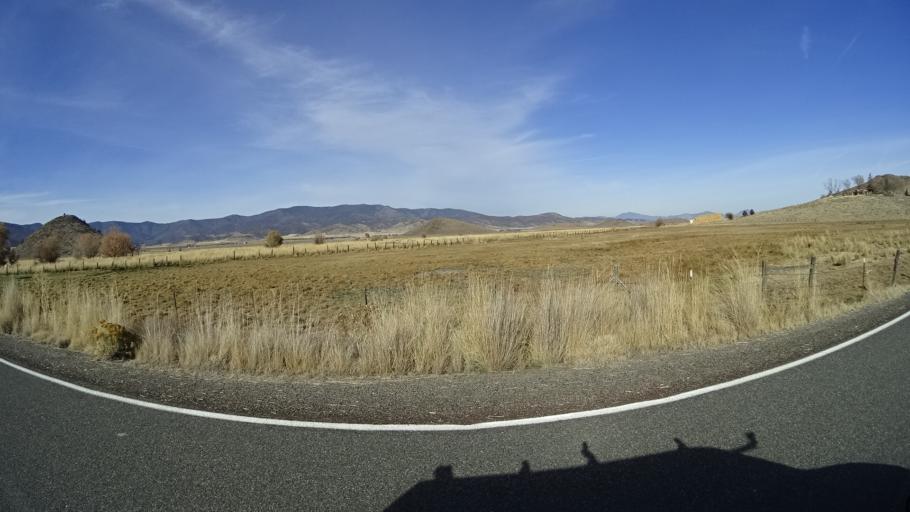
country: US
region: California
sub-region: Siskiyou County
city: Weed
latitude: 41.5350
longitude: -122.5109
